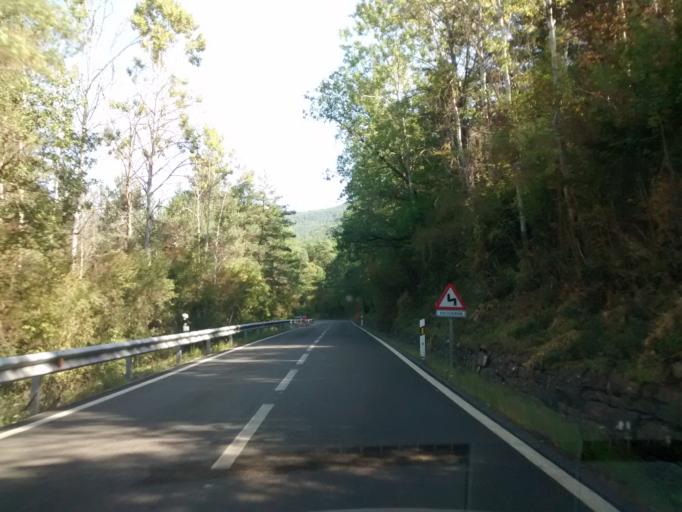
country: ES
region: Aragon
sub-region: Provincia de Huesca
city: Fiscal
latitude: 42.5438
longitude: -0.1302
